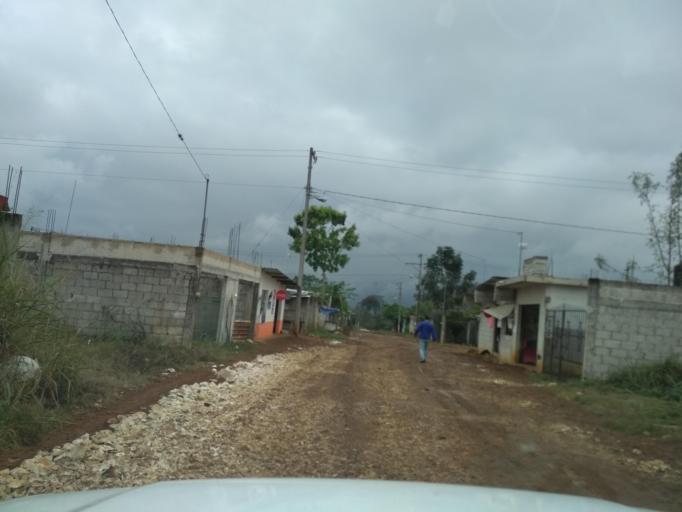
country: MX
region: Veracruz
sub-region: Cordoba
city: San Jose de Tapia
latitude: 18.8444
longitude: -96.9658
